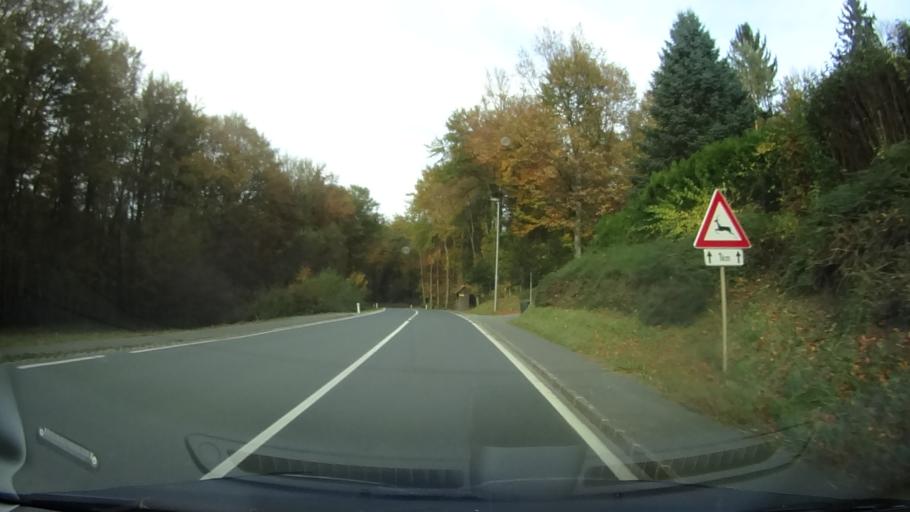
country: AT
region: Styria
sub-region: Politischer Bezirk Deutschlandsberg
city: Wettmannstatten
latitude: 46.8057
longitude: 15.3939
